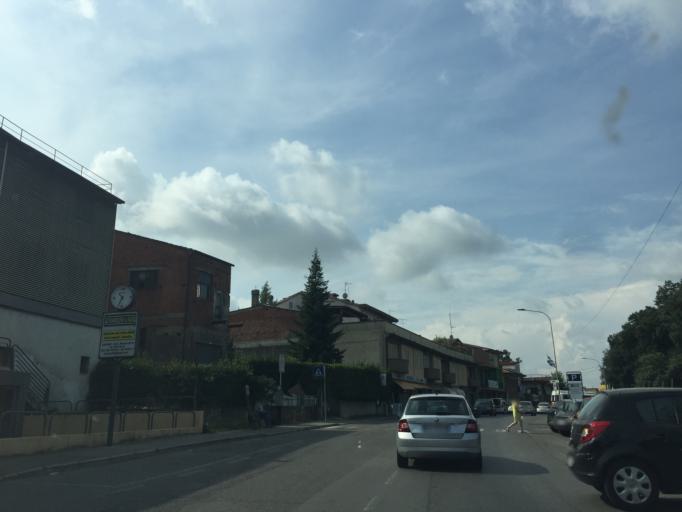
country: IT
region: Tuscany
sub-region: Provincia di Pistoia
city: Larciano
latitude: 43.8162
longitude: 10.8953
